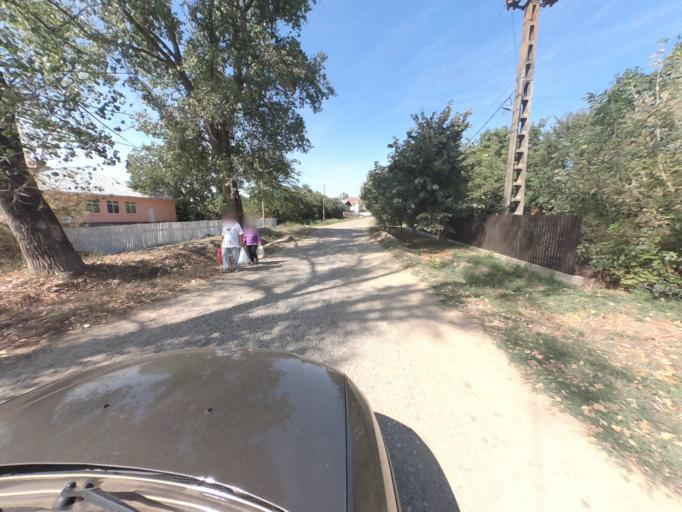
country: RO
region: Vaslui
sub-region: Comuna Deleni
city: Deleni
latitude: 46.5407
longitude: 27.7474
